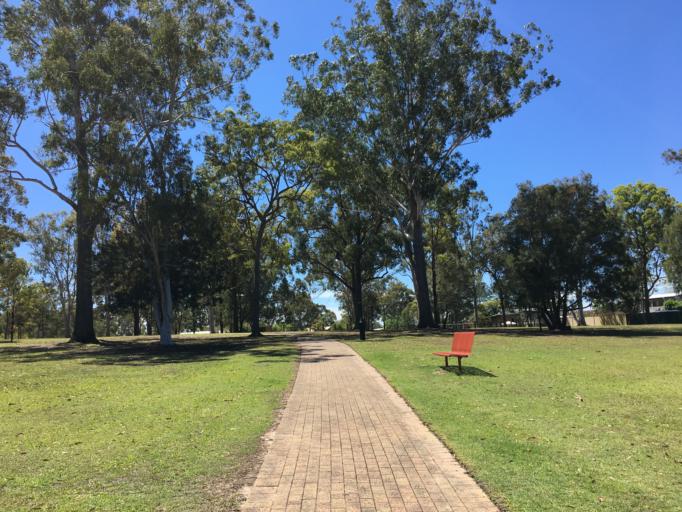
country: AU
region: Queensland
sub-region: Logan
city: Logan City
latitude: -27.6486
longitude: 153.1057
